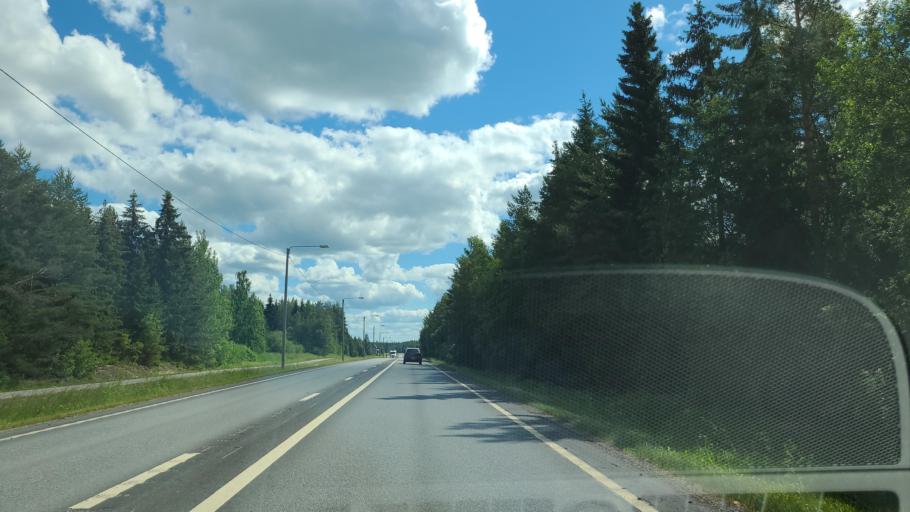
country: FI
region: Ostrobothnia
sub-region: Kyroenmaa
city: Isokyroe
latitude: 62.9806
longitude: 22.3432
